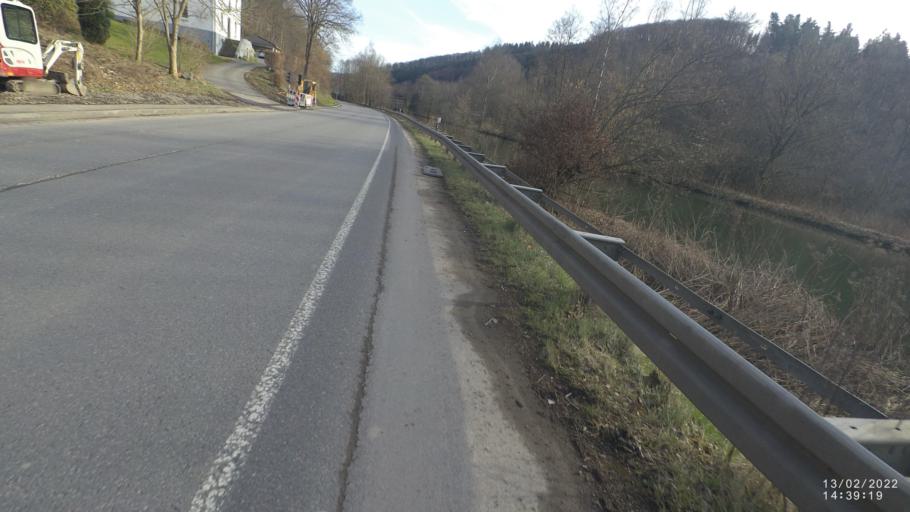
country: DE
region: North Rhine-Westphalia
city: Werdohl
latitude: 51.2673
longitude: 7.7257
